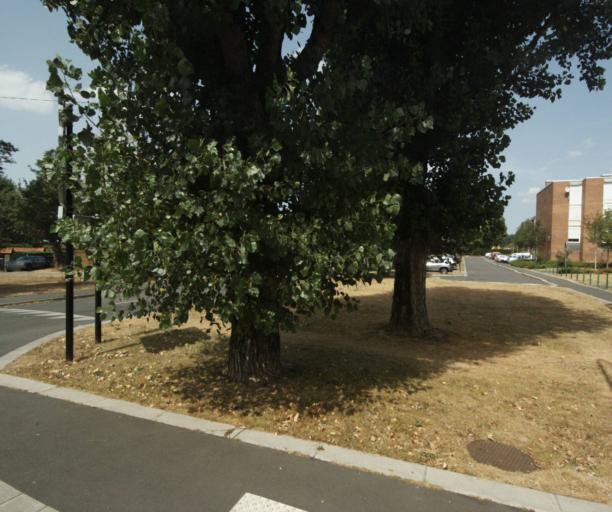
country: FR
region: Nord-Pas-de-Calais
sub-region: Departement du Nord
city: Wattrelos
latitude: 50.7007
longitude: 3.2326
